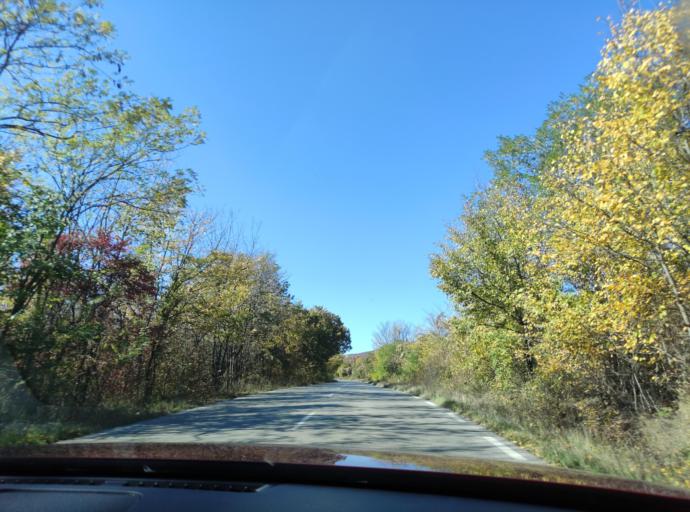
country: BG
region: Montana
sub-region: Obshtina Chiprovtsi
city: Chiprovtsi
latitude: 43.4312
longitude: 22.9920
